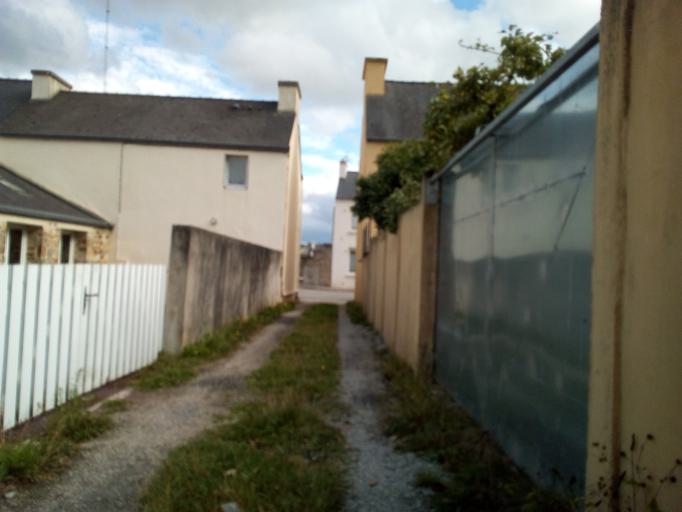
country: FR
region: Brittany
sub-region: Departement du Finistere
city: Landivisiau
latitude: 48.5123
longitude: -4.0650
